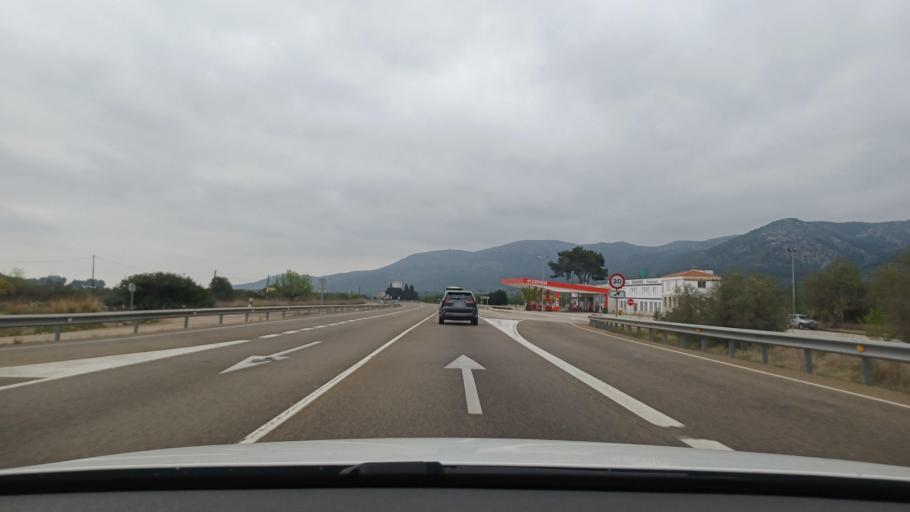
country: ES
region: Valencia
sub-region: Provincia de Castello
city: Santa Magdalena de Pulpis
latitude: 40.3598
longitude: 0.3016
